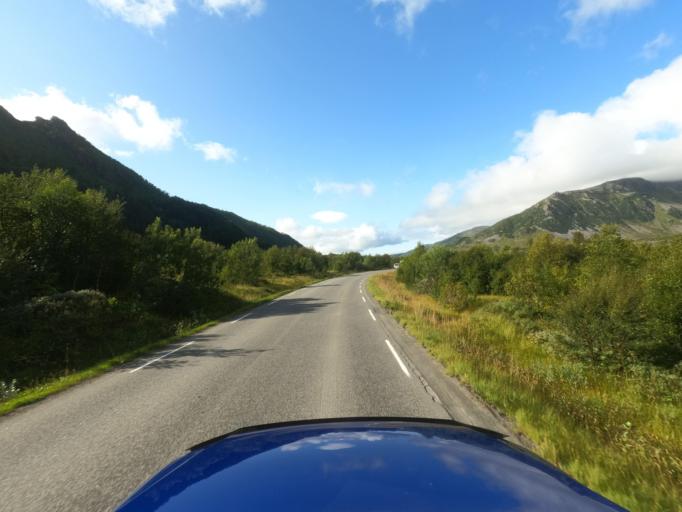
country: NO
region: Nordland
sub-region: Vestvagoy
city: Evjen
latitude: 68.1542
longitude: 13.8202
